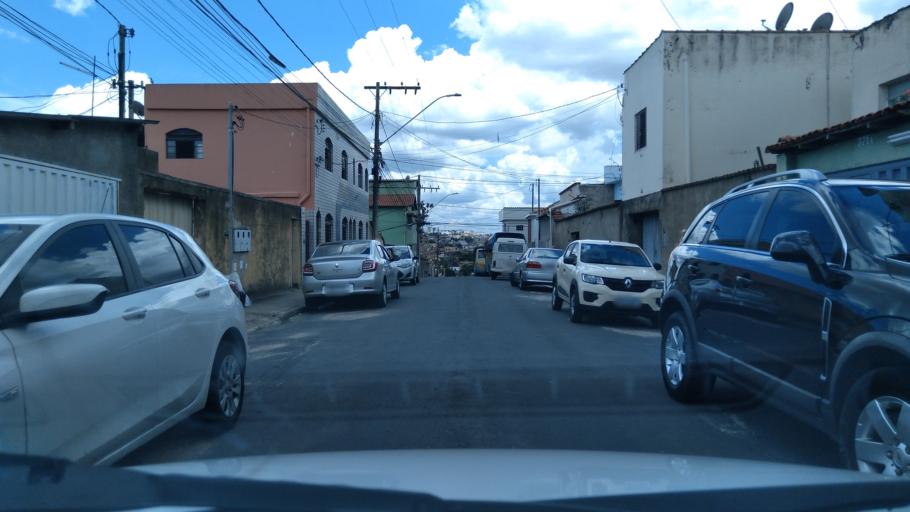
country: BR
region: Minas Gerais
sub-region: Belo Horizonte
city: Belo Horizonte
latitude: -19.9145
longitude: -43.8987
